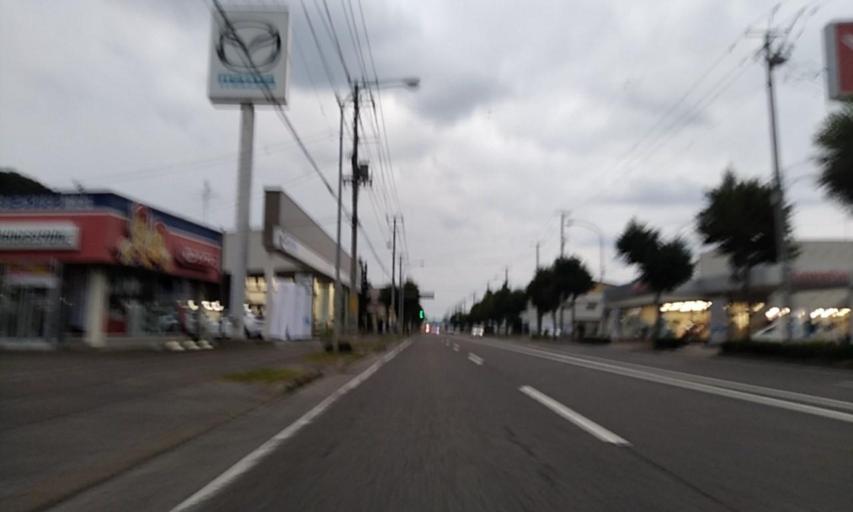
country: JP
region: Hokkaido
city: Abashiri
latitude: 44.0169
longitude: 144.2427
